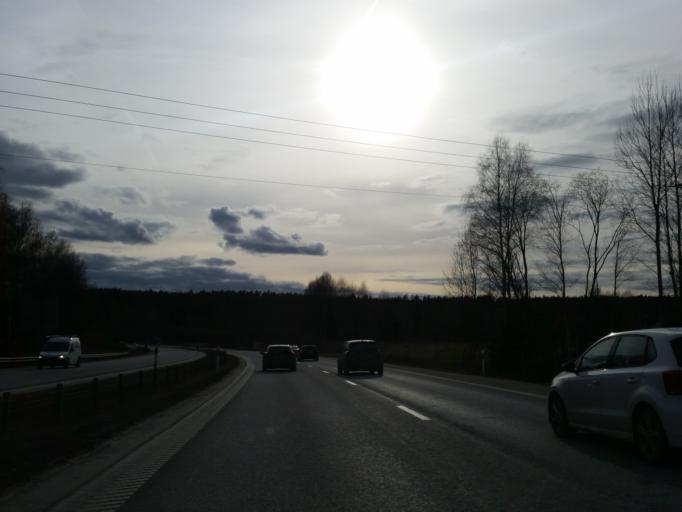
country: SE
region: OEstergoetland
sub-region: Norrkopings Kommun
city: Krokek
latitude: 58.7043
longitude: 16.3452
